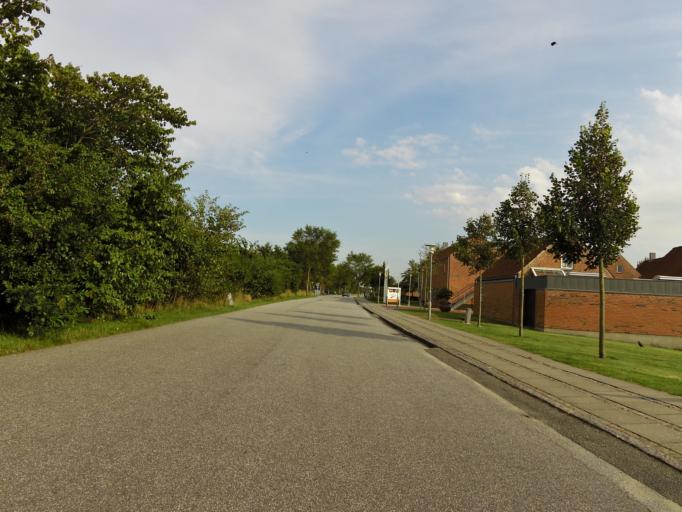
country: DK
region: South Denmark
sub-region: Esbjerg Kommune
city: Ribe
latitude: 55.3245
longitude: 8.7612
